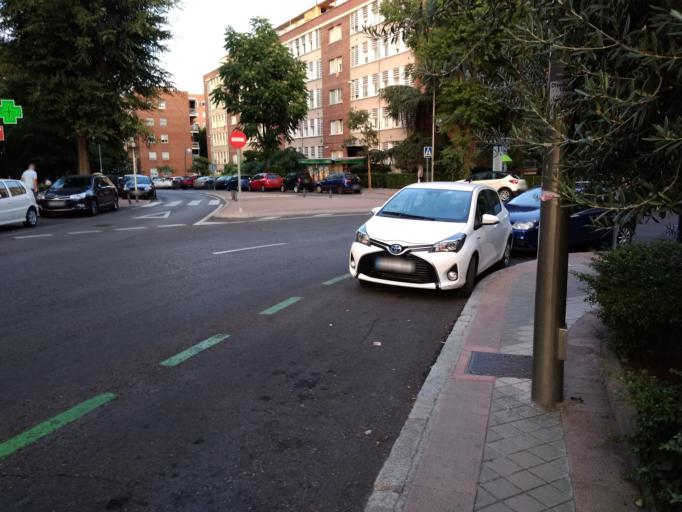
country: ES
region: Madrid
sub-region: Provincia de Madrid
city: Retiro
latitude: 40.4127
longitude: -3.6682
